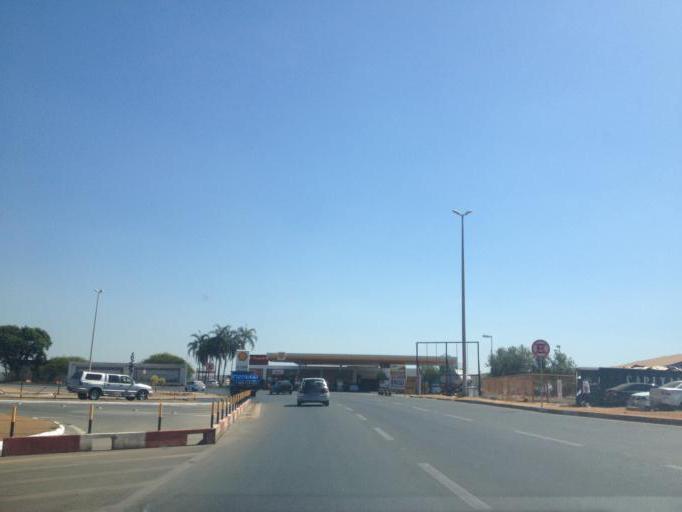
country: BR
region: Federal District
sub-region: Brasilia
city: Brasilia
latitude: -15.8681
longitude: -47.9233
